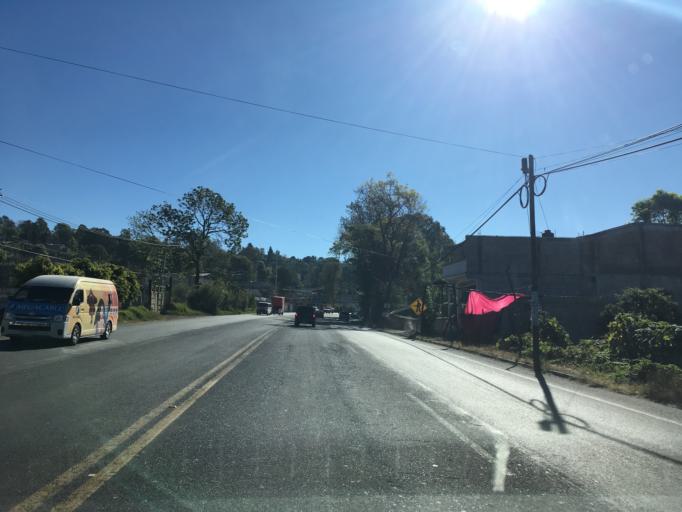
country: MX
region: Michoacan
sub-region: Zitacuaro
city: Valle Verde
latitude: 19.4736
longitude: -100.3481
